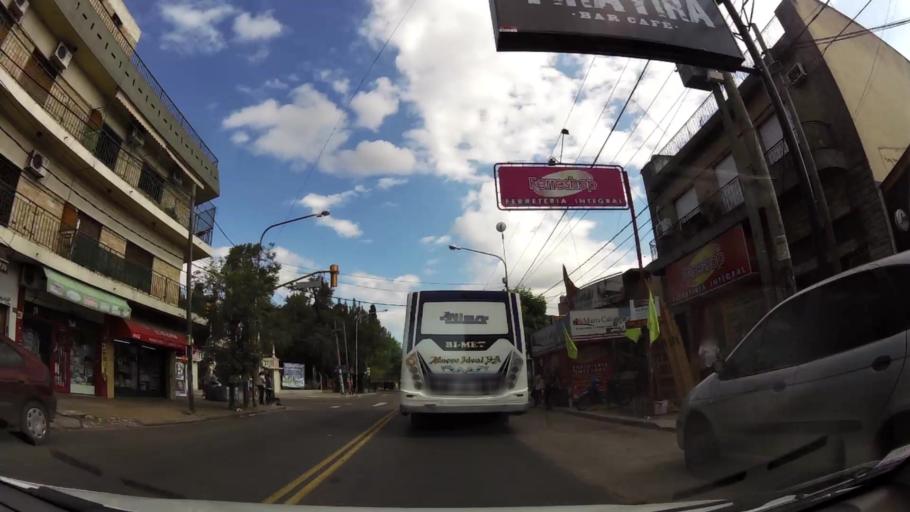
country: AR
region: Buenos Aires
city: San Justo
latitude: -34.6603
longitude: -58.5620
